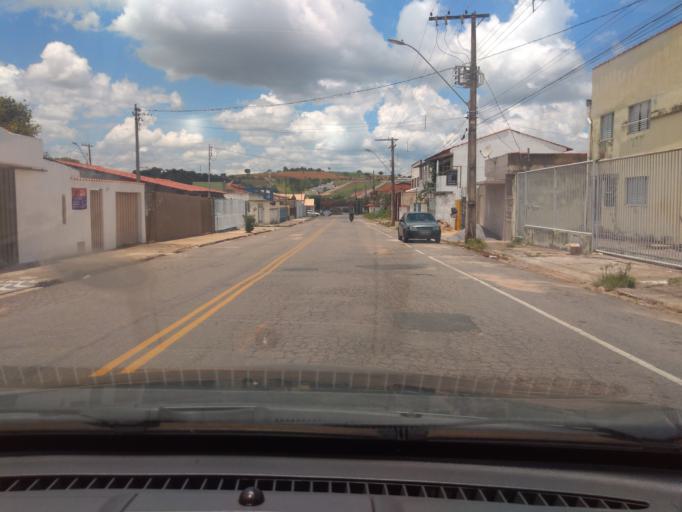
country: BR
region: Minas Gerais
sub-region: Tres Coracoes
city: Tres Coracoes
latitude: -21.6761
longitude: -45.2677
